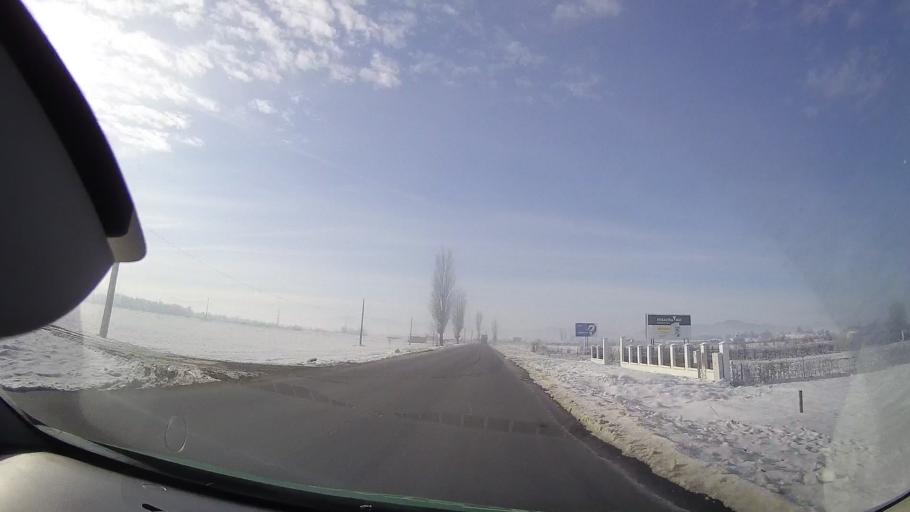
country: RO
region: Neamt
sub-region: Comuna Raucesti
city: Raucesti
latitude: 47.2103
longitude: 26.4180
